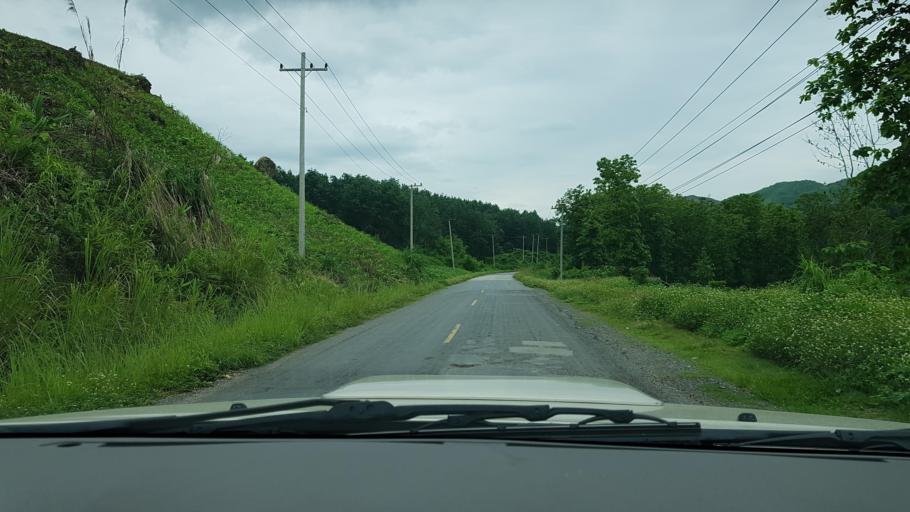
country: LA
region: Loungnamtha
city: Muang Nale
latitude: 20.2013
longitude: 101.5310
